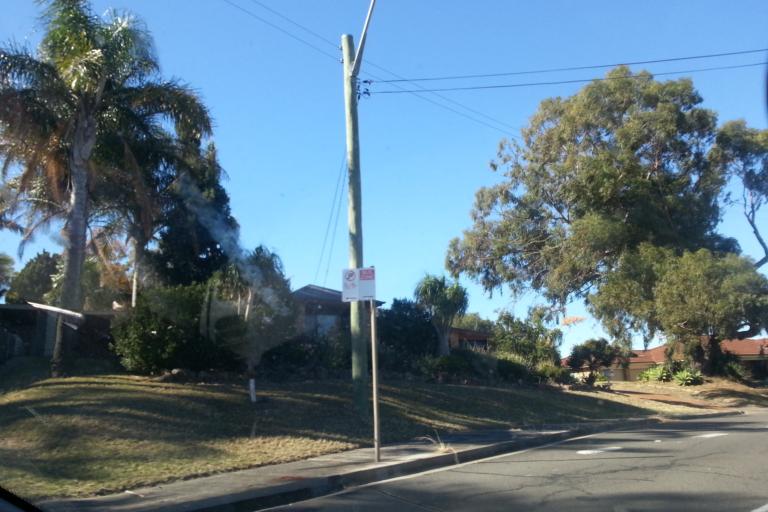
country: AU
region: New South Wales
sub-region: Wollongong
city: Dapto
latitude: -34.5093
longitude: 150.7865
